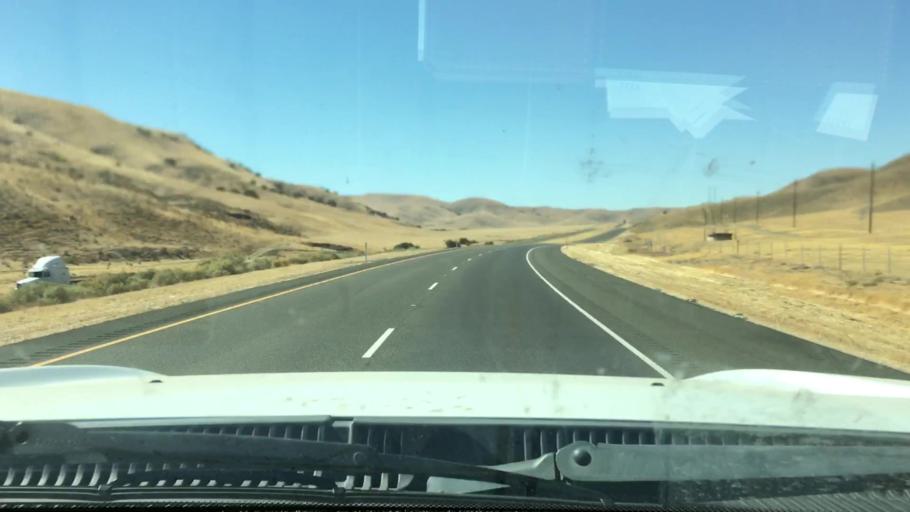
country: US
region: California
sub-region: San Luis Obispo County
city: Shandon
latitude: 35.7116
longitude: -120.1633
